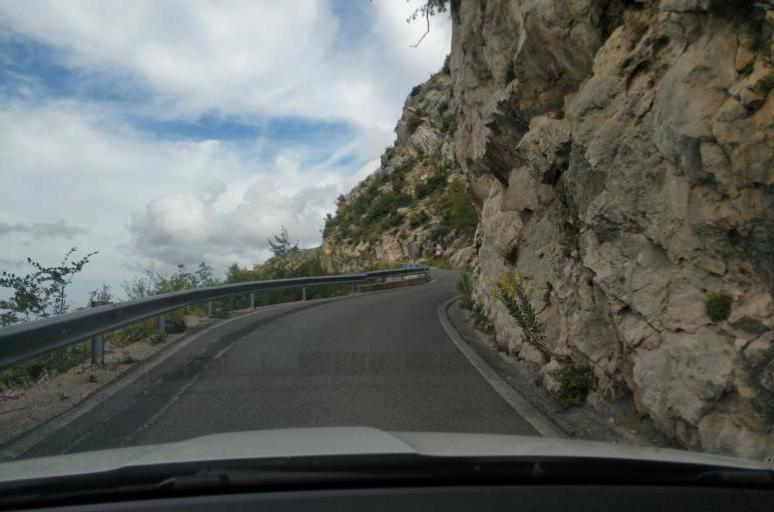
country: AL
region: Durres
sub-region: Rrethi i Krujes
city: Kruje
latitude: 41.5259
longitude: 19.7944
